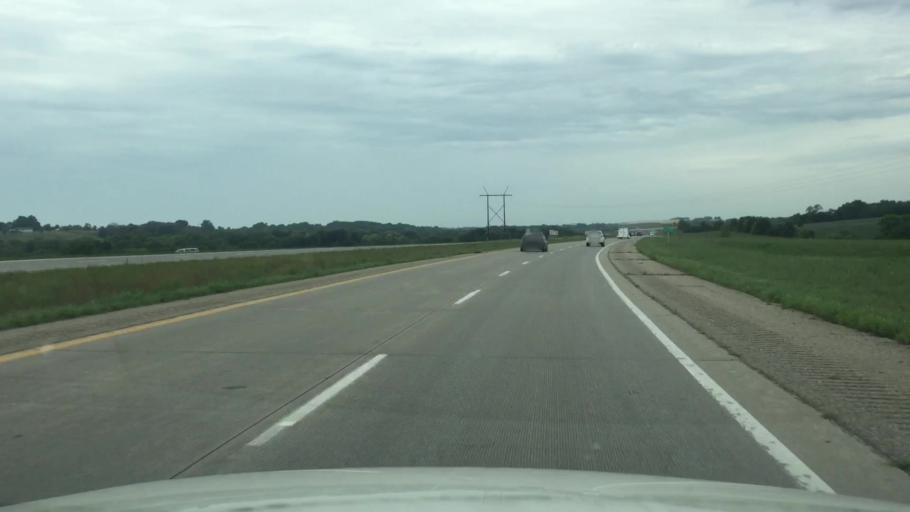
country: US
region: Iowa
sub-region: Warren County
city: Norwalk
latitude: 41.4995
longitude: -93.6273
